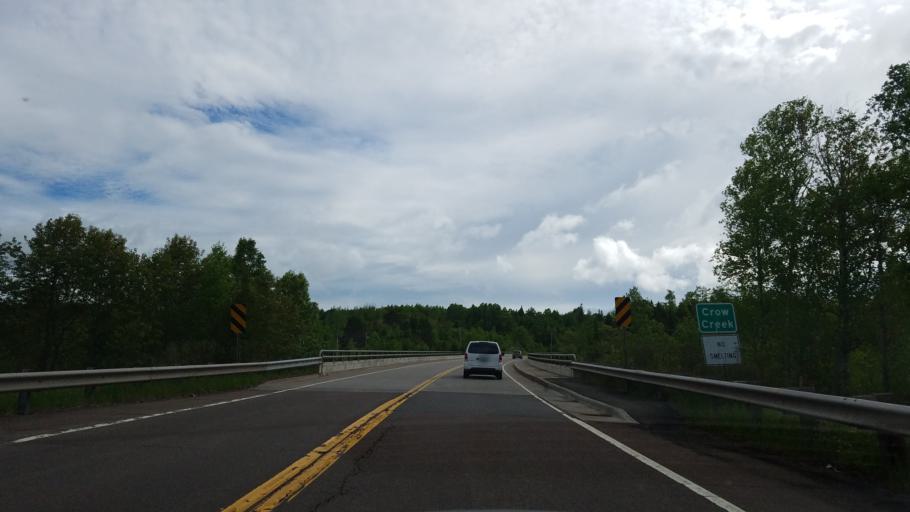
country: US
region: Minnesota
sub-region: Lake County
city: Two Harbors
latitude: 47.1004
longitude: -91.5467
